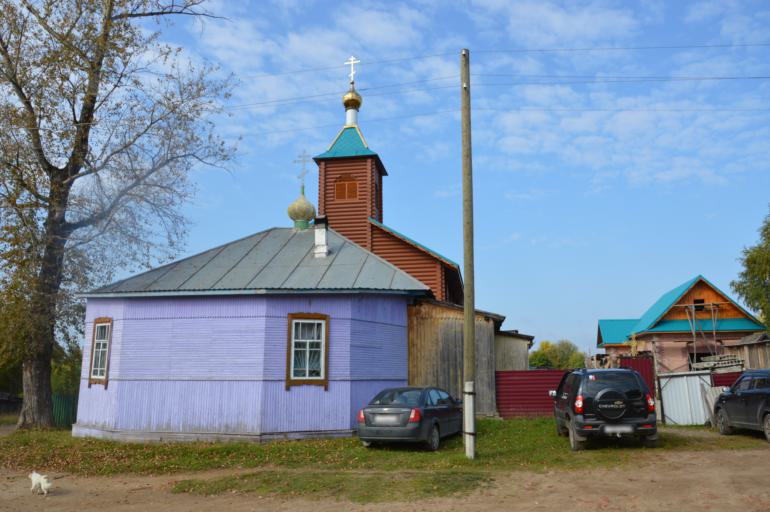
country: RU
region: Kirov
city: Peskovka
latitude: 59.0459
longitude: 52.3569
